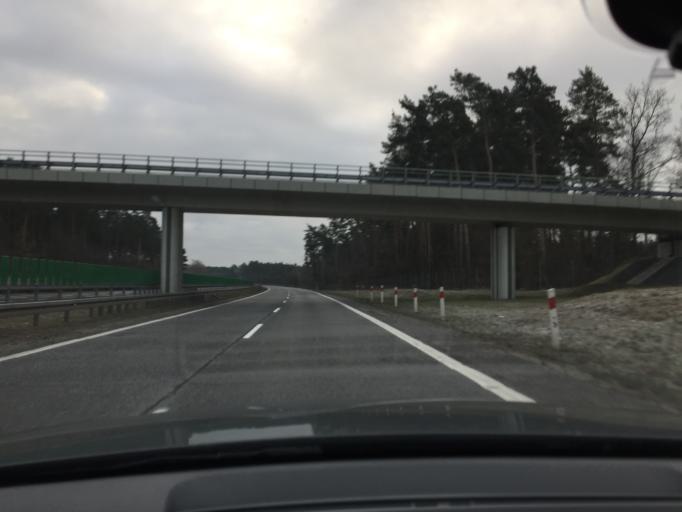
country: PL
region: Lubusz
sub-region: Powiat zarski
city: Trzebiel
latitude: 51.6478
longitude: 14.8293
